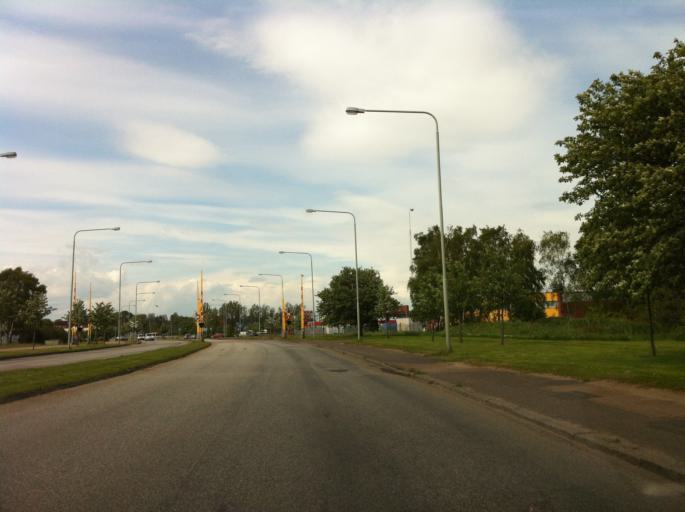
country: SE
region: Skane
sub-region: Landskrona
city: Landskrona
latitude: 55.8690
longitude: 12.8512
